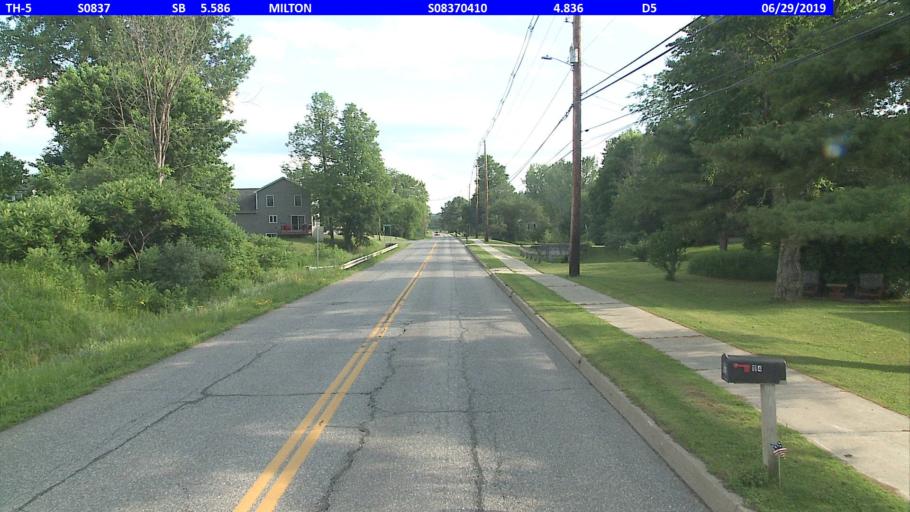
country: US
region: Vermont
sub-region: Chittenden County
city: Milton
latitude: 44.6426
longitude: -73.1001
